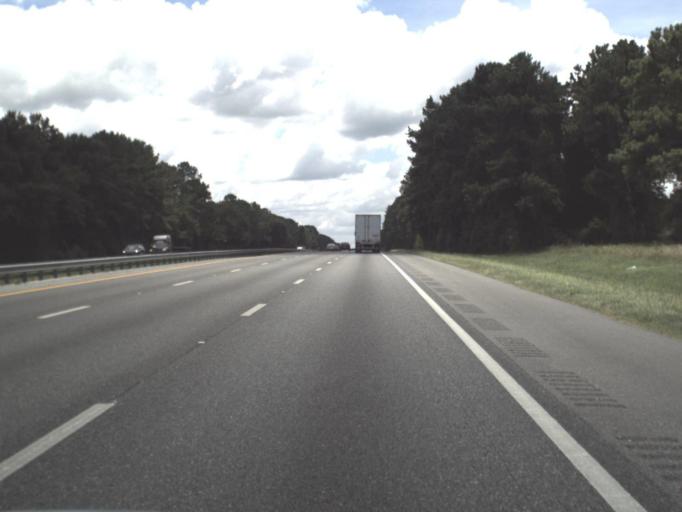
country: US
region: Florida
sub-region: Alachua County
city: High Springs
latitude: 29.9593
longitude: -82.5715
